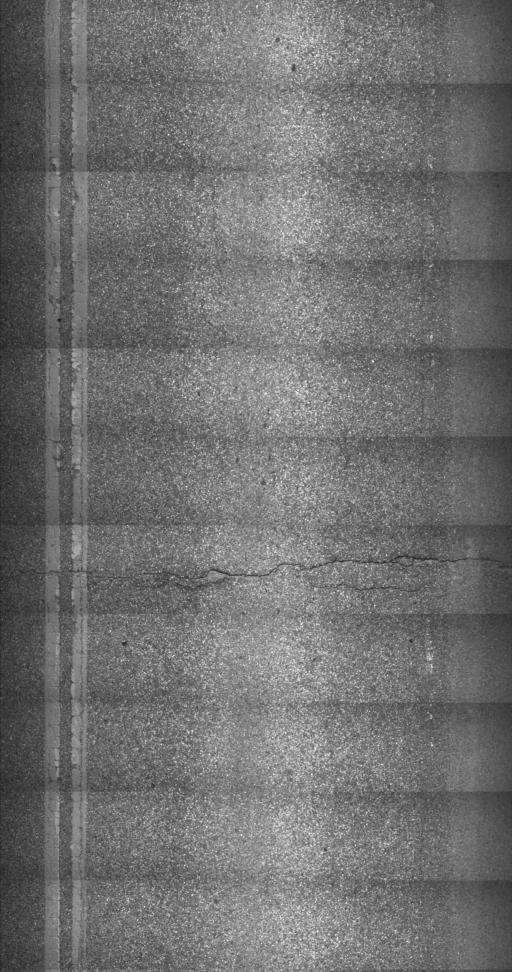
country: US
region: Vermont
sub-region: Bennington County
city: North Bennington
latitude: 42.9184
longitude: -73.2470
